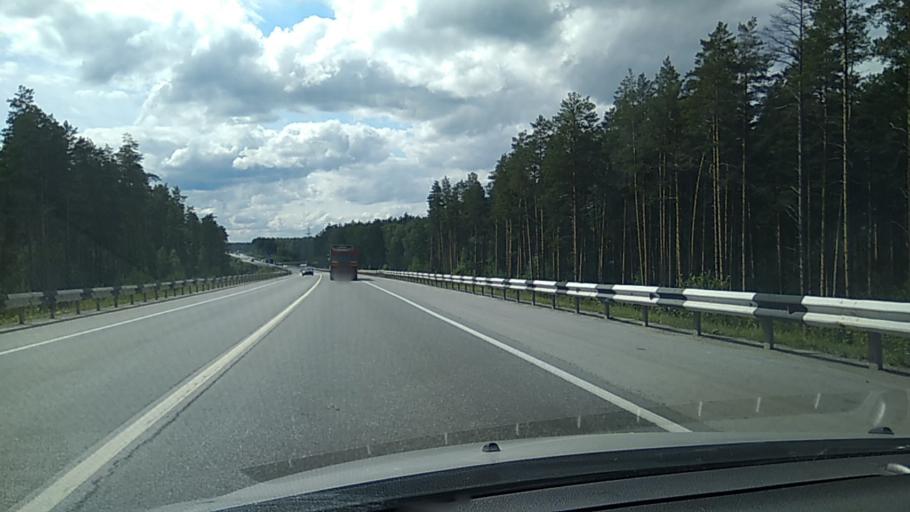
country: RU
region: Sverdlovsk
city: Verkhnyaya Pyshma
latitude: 56.9396
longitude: 60.5340
